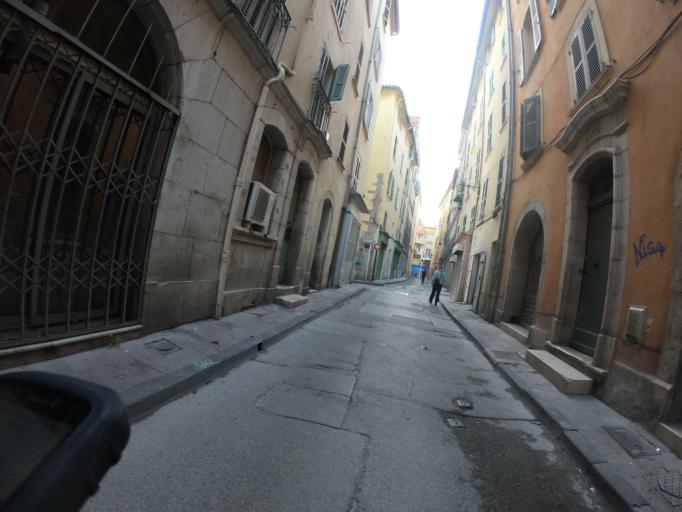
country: FR
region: Provence-Alpes-Cote d'Azur
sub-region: Departement du Var
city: Toulon
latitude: 43.1214
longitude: 5.9357
